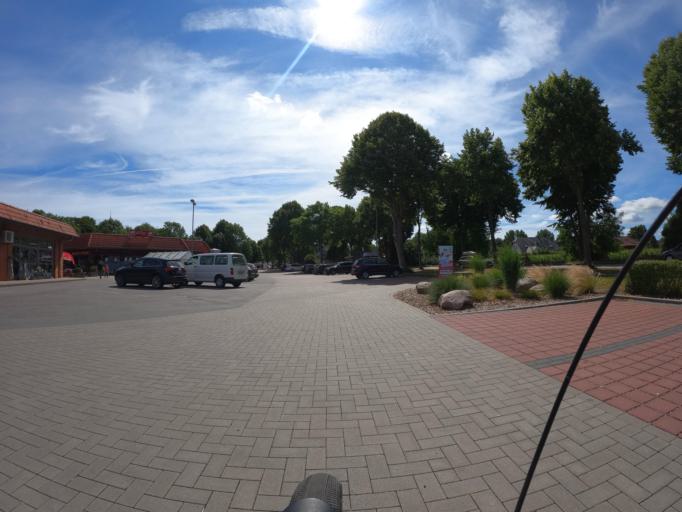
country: DE
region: Schleswig-Holstein
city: Steinbergkirche
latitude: 54.7555
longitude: 9.7569
